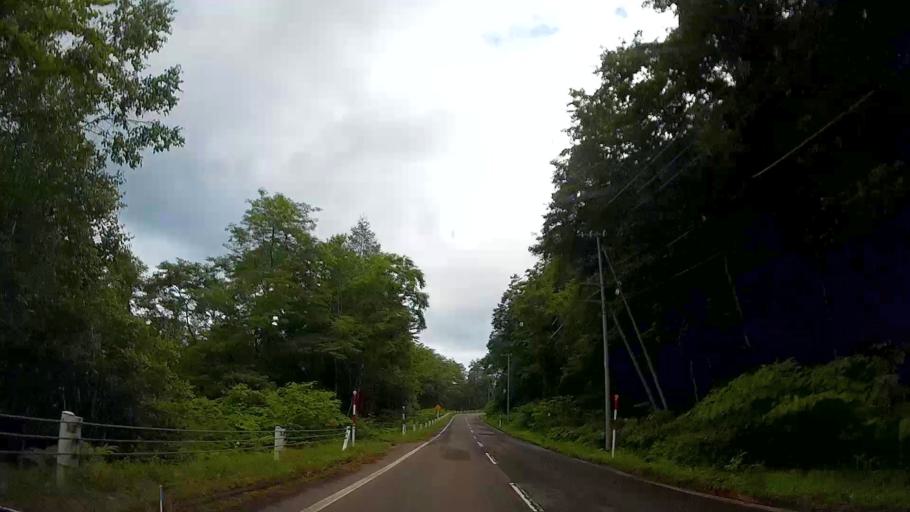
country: JP
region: Hokkaido
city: Nanae
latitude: 42.0851
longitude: 140.5496
